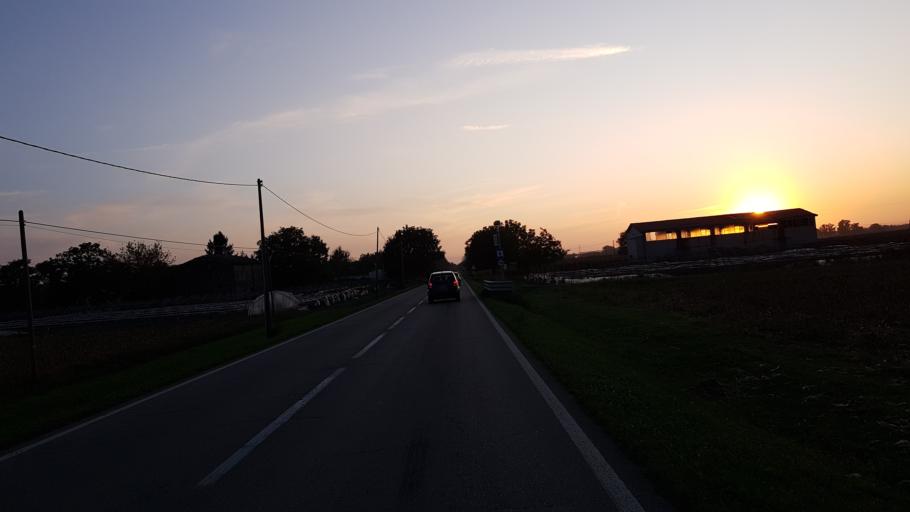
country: IT
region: Emilia-Romagna
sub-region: Provincia di Modena
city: Camposanto
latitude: 44.7917
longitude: 11.1641
